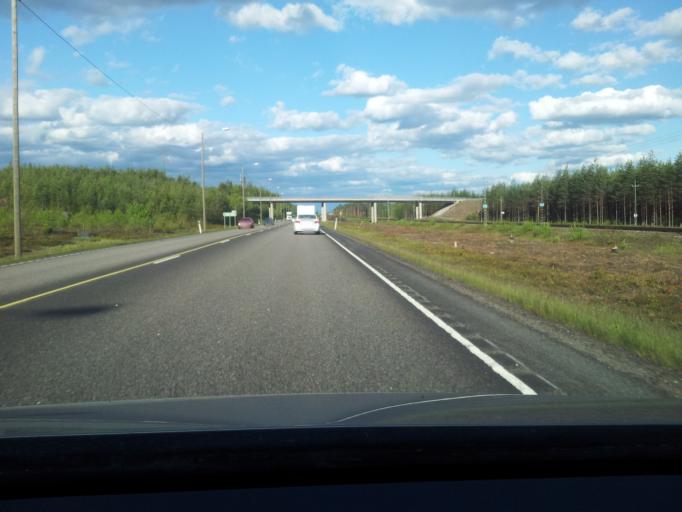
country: FI
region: Kymenlaakso
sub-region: Kotka-Hamina
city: Hamina
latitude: 60.9040
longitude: 27.1990
